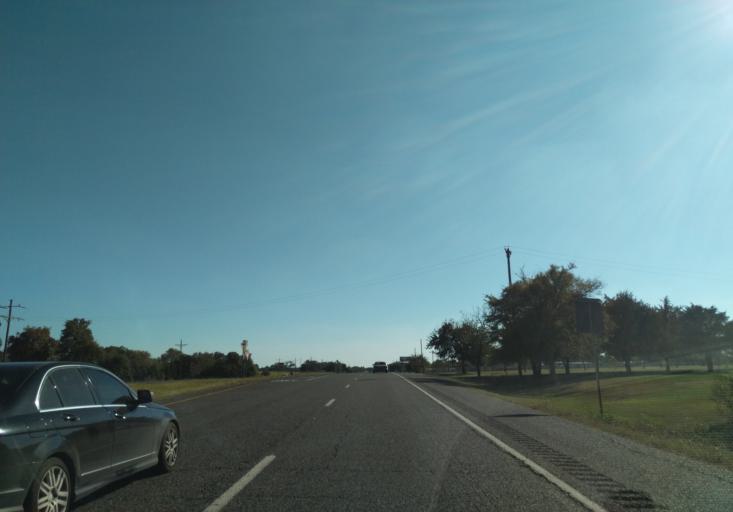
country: US
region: Texas
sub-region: Waller County
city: Hempstead
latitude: 30.2104
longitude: -96.0583
